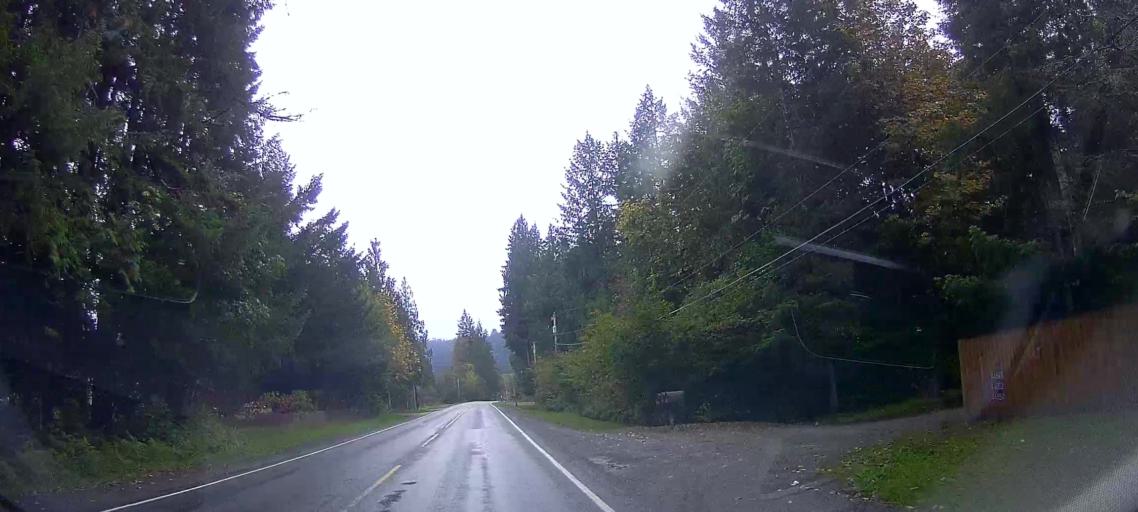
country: US
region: Washington
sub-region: Snohomish County
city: Darrington
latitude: 48.5304
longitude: -121.7662
